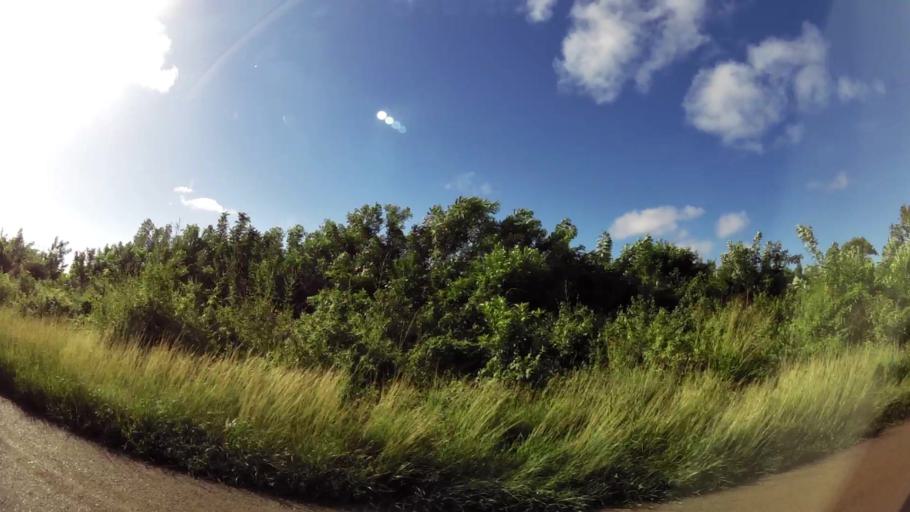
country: TT
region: Tobago
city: Scarborough
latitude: 11.1492
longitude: -60.8385
